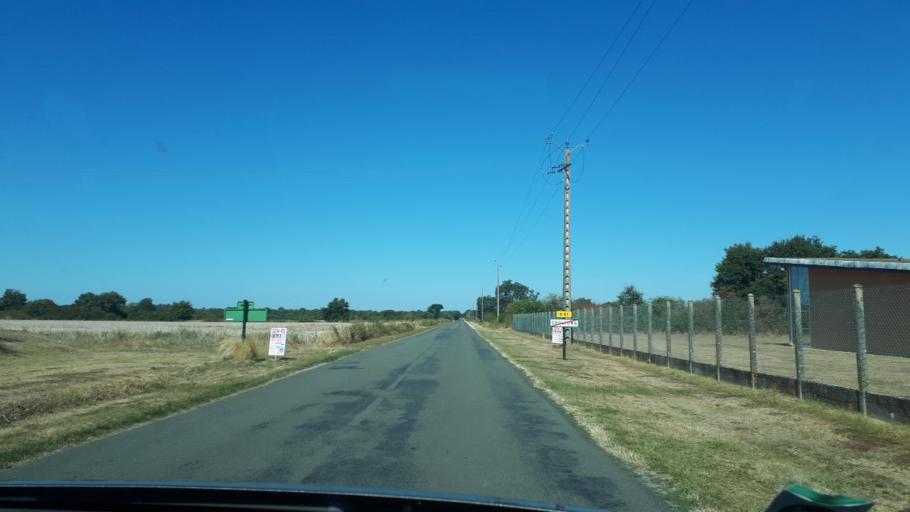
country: FR
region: Centre
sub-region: Departement du Loiret
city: Coullons
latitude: 47.6266
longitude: 2.4850
